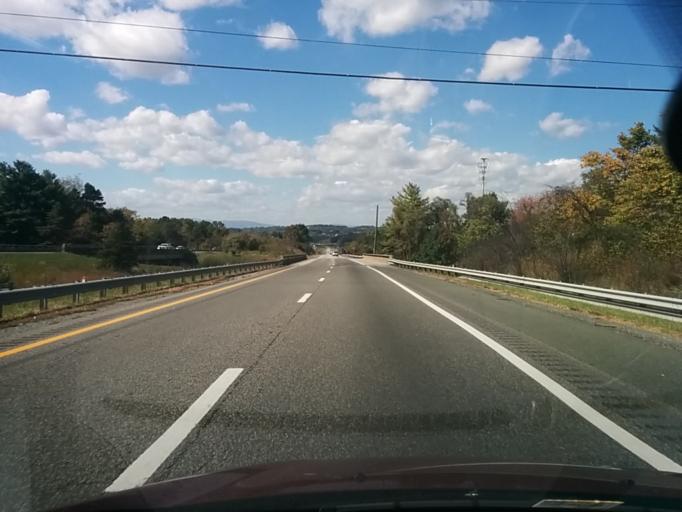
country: US
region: Virginia
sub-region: City of Waynesboro
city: Waynesboro
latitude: 38.0467
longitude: -78.9049
